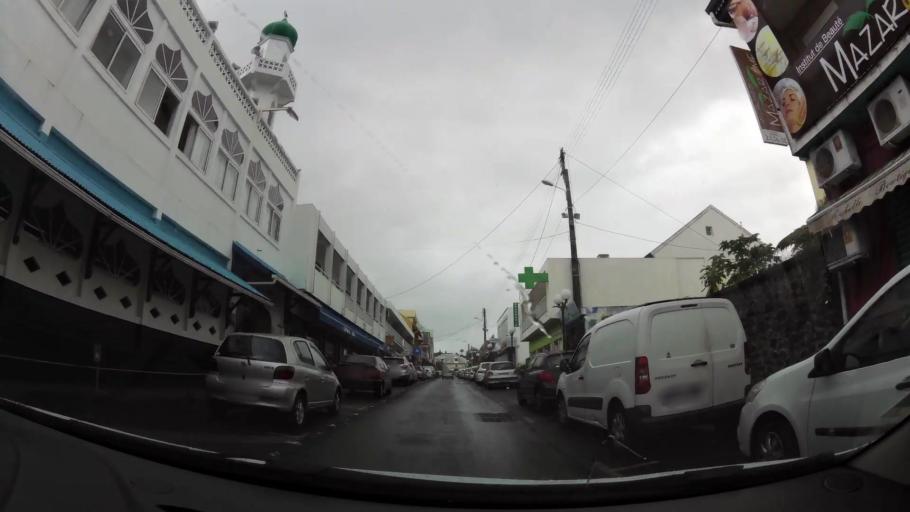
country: RE
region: Reunion
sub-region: Reunion
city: Saint-Andre
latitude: -20.9586
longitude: 55.6499
